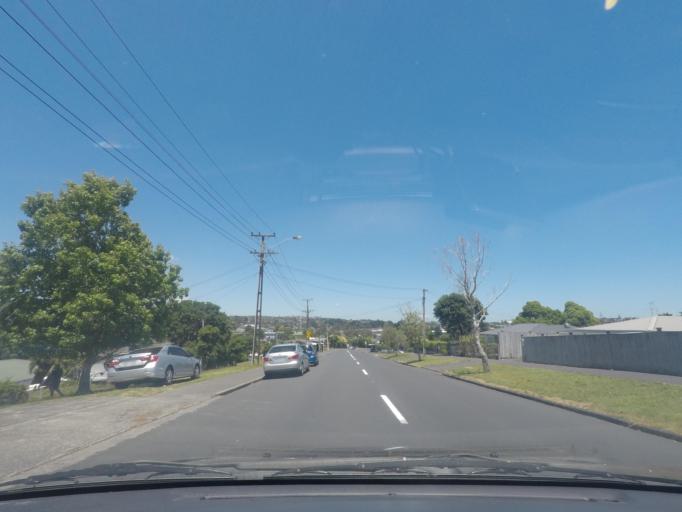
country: NZ
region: Auckland
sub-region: Auckland
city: Rosebank
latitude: -36.9101
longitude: 174.7163
